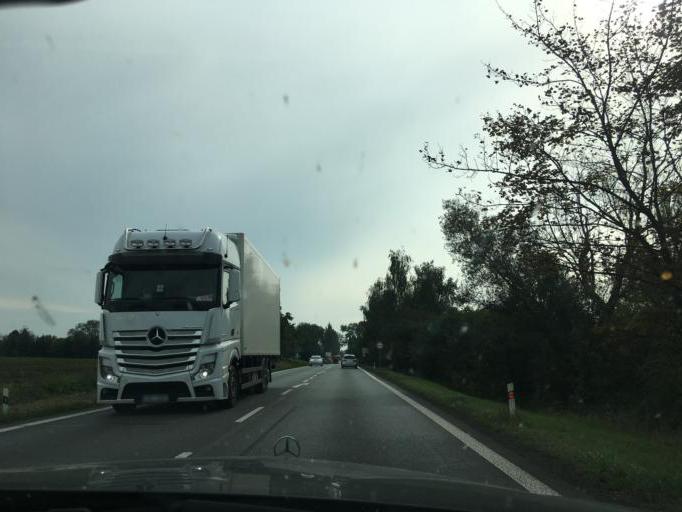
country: CZ
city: Predmerice nad Labem
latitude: 50.2460
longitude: 15.7989
